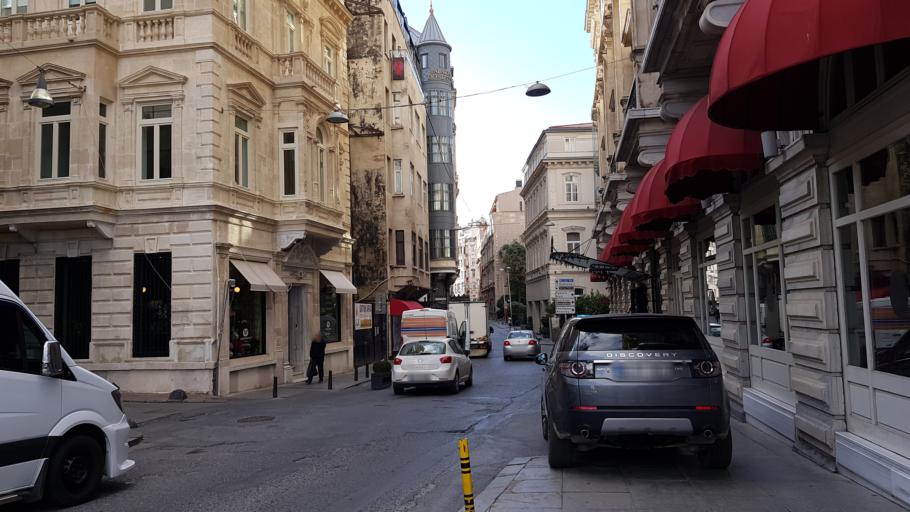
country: TR
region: Istanbul
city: Eminoenue
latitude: 41.0312
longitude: 28.9738
